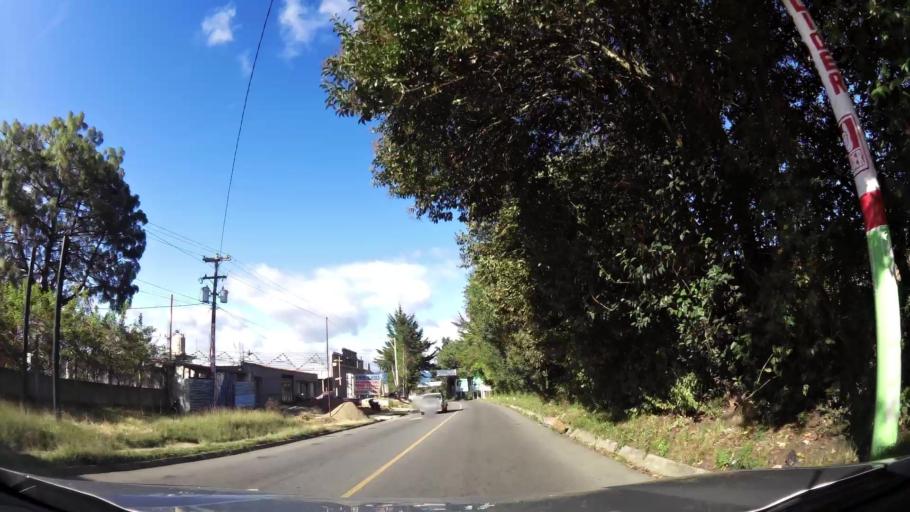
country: GT
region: Quiche
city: Chichicastenango
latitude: 14.9552
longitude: -91.1063
